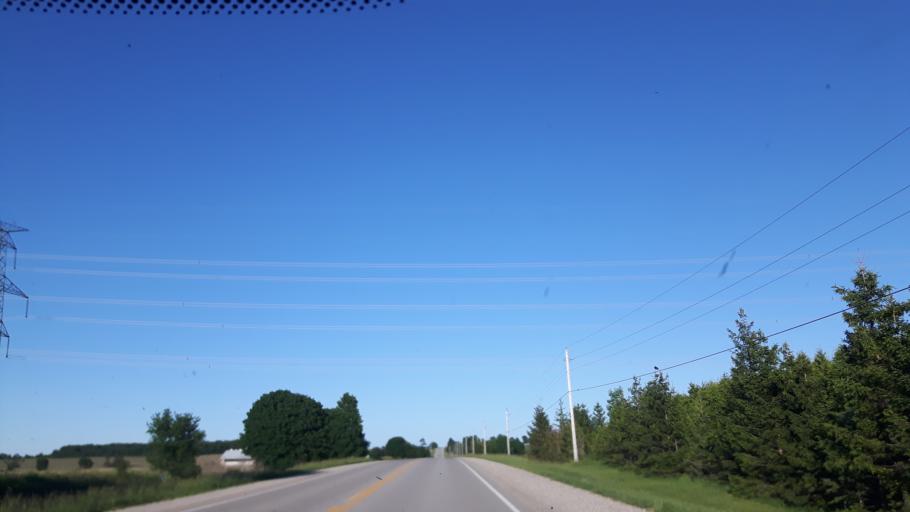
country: CA
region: Ontario
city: Goderich
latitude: 43.6426
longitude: -81.6336
